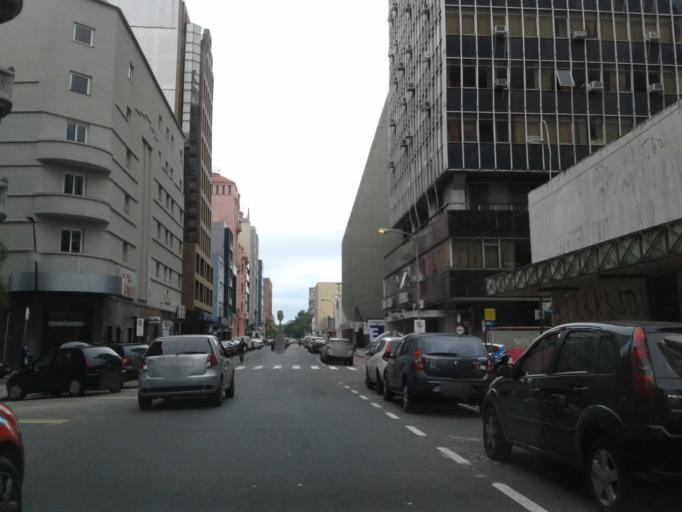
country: BR
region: Rio Grande do Sul
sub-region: Porto Alegre
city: Porto Alegre
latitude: -30.0303
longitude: -51.2334
